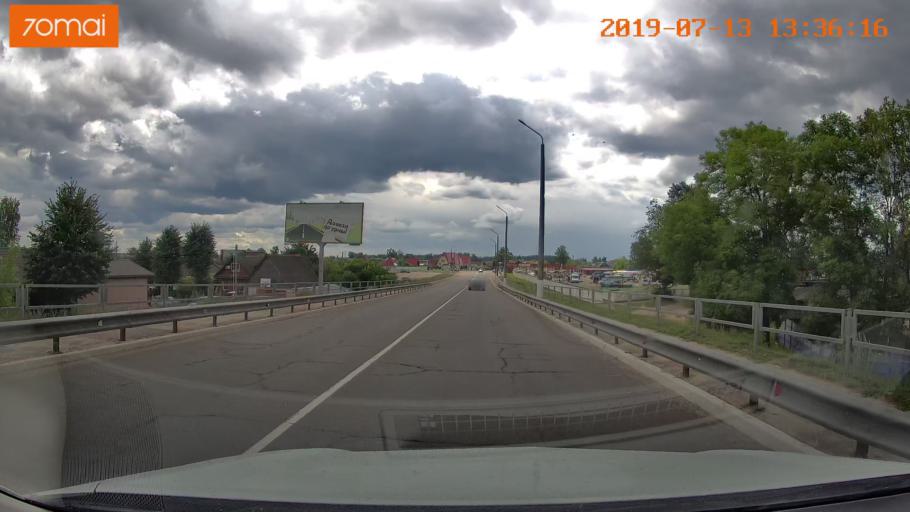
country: BY
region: Mogilev
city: Asipovichy
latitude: 53.3034
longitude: 28.6233
